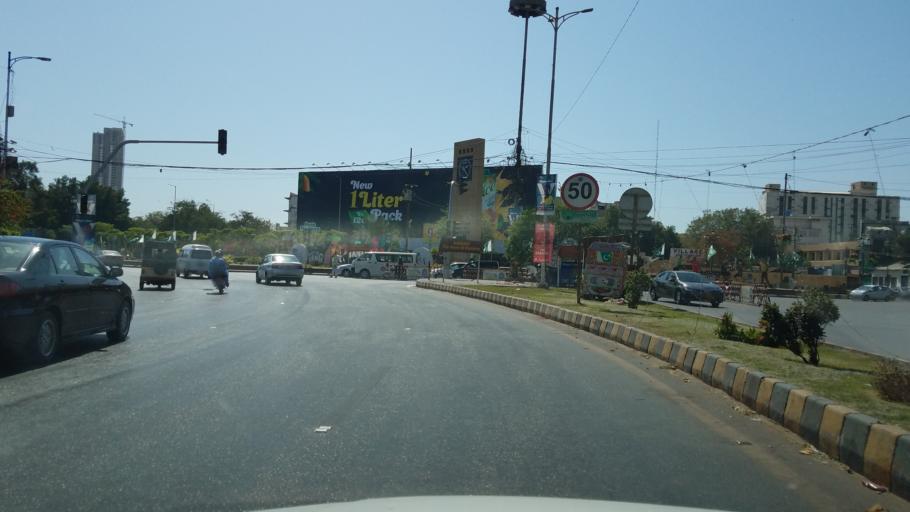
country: PK
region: Sindh
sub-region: Karachi District
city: Karachi
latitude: 24.8515
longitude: 67.0325
